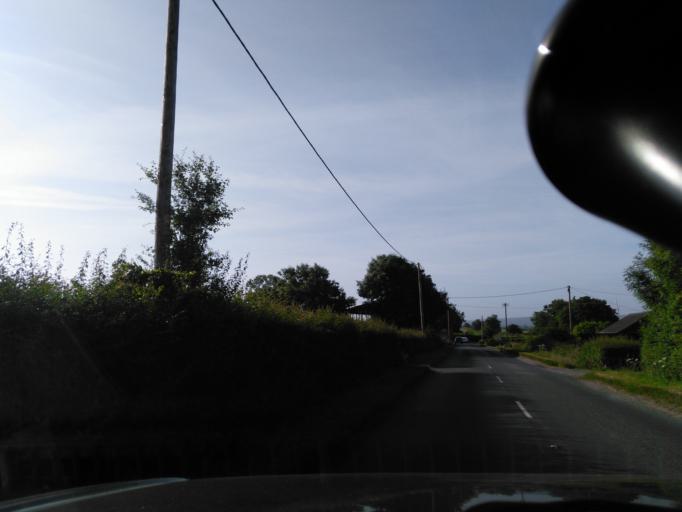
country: GB
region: England
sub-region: Wiltshire
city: Seend
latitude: 51.3430
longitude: -2.0851
